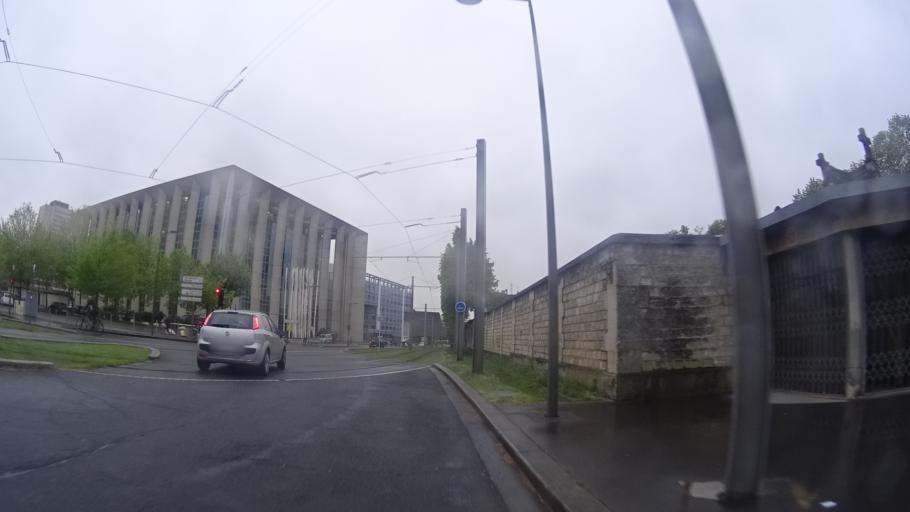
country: FR
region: Aquitaine
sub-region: Departement de la Gironde
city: Bordeaux
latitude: 44.8372
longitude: -0.5900
